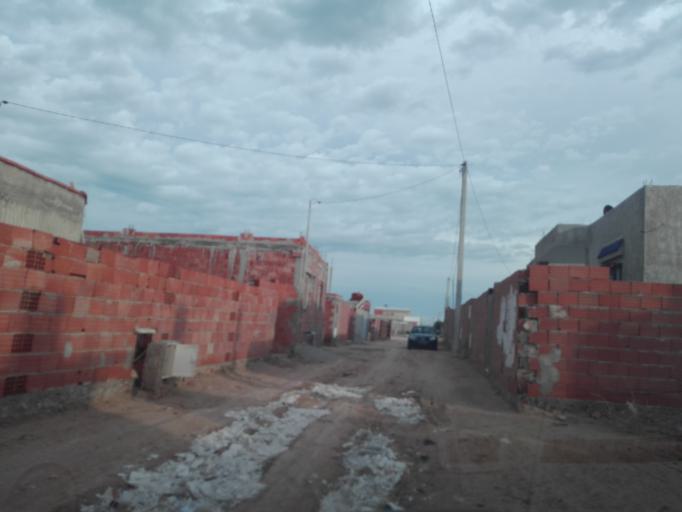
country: TN
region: Safaqis
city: Al Qarmadah
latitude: 34.8084
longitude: 10.8593
